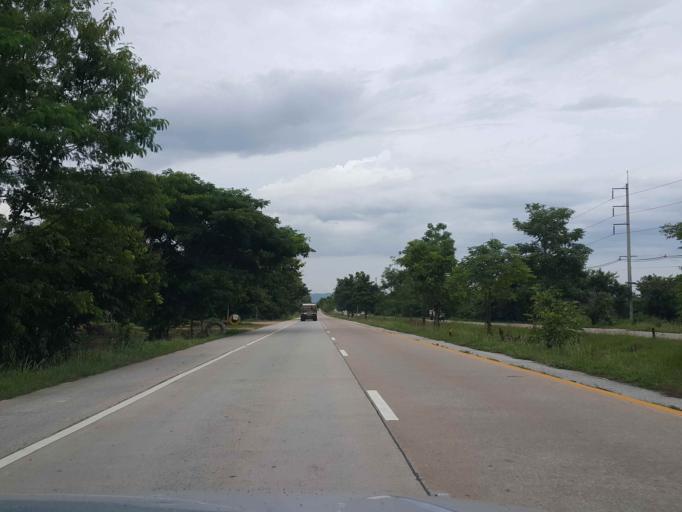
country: TH
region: Lampang
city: Hang Chat
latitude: 18.3012
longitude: 99.4066
